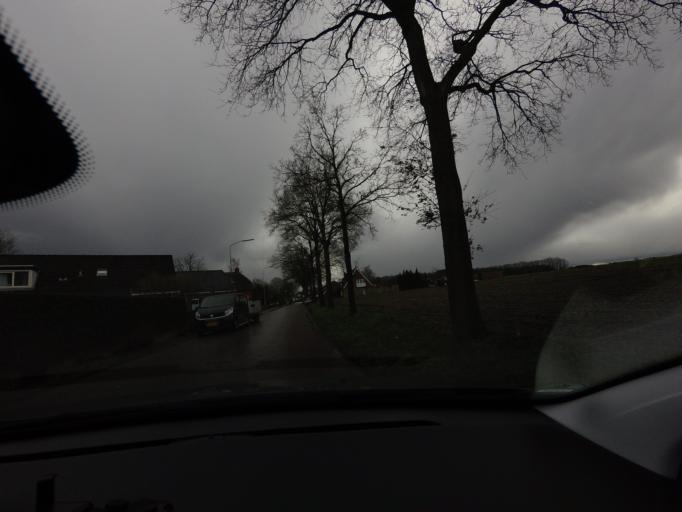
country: NL
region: Drenthe
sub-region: Gemeente Borger-Odoorn
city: Borger
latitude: 52.9299
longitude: 6.7901
